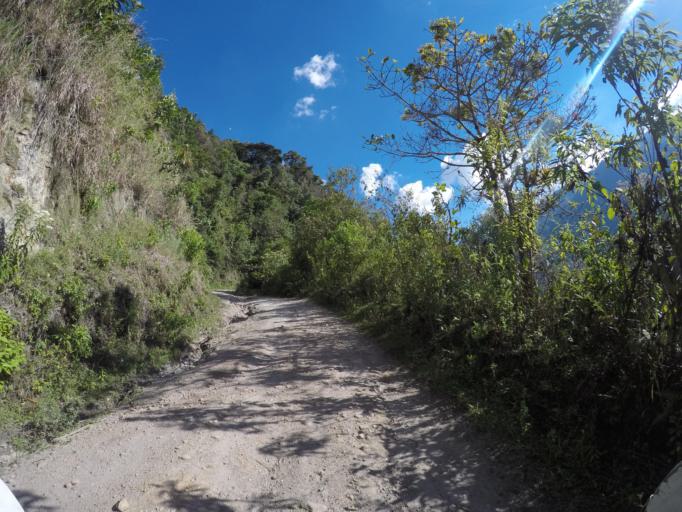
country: CO
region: Tolima
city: Cajamarca
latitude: 4.5182
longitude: -75.4068
